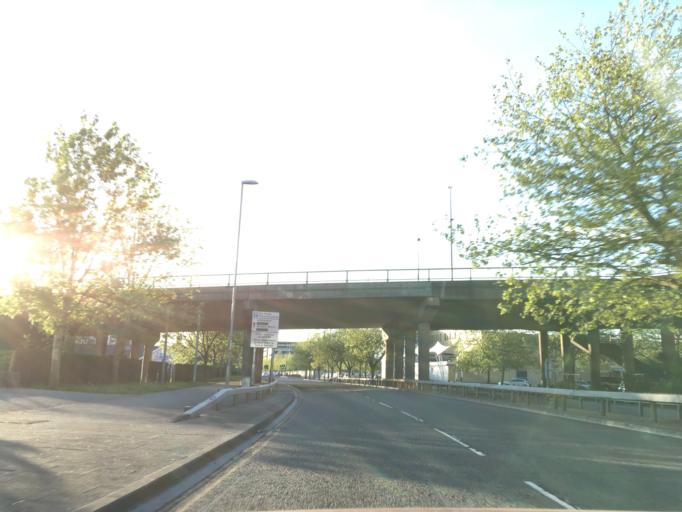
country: GB
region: Wales
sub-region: Newport
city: Newport
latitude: 51.5826
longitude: -2.9862
